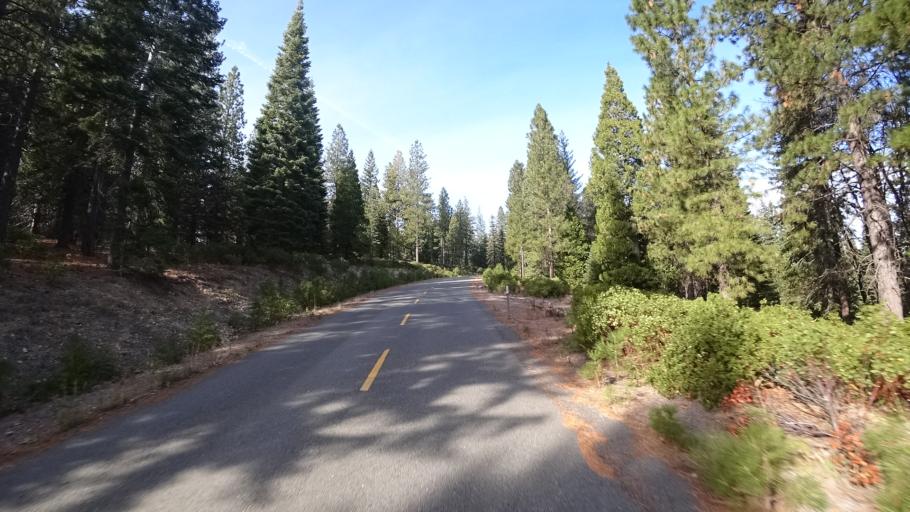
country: US
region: California
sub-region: Siskiyou County
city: Weed
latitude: 41.3937
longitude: -122.3923
